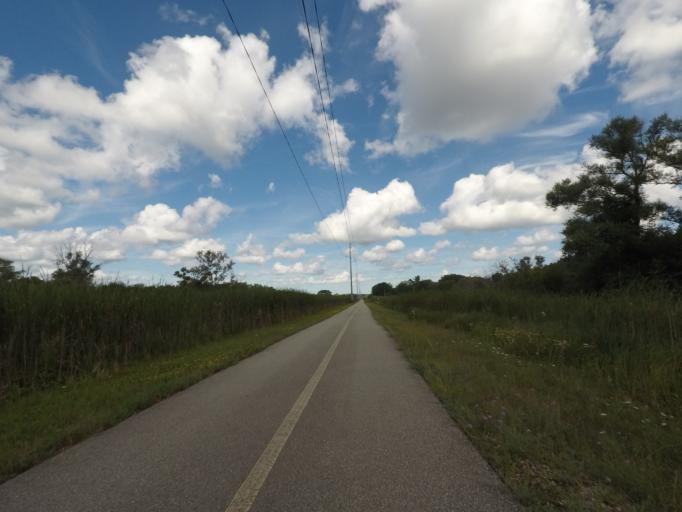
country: US
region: Wisconsin
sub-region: Waukesha County
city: Pewaukee
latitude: 43.0529
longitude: -88.2825
